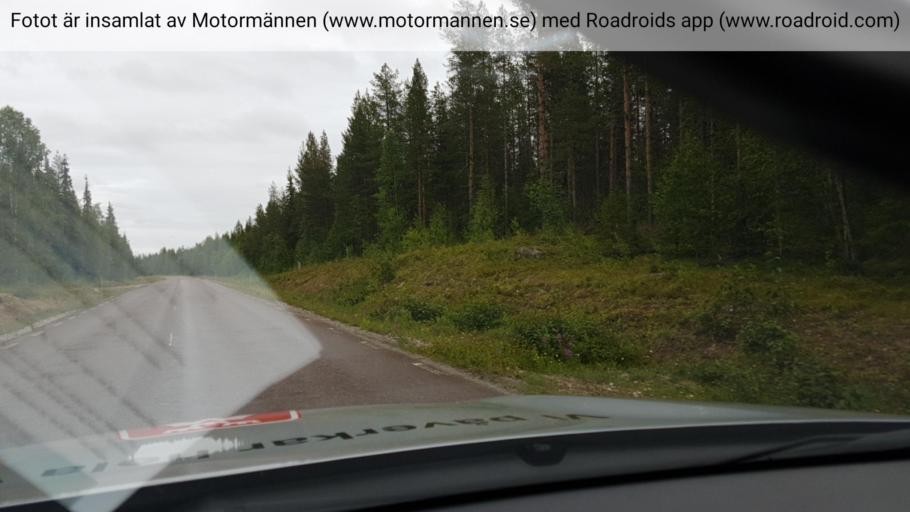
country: SE
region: Norrbotten
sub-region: Overkalix Kommun
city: OEverkalix
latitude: 67.0664
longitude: 22.3975
